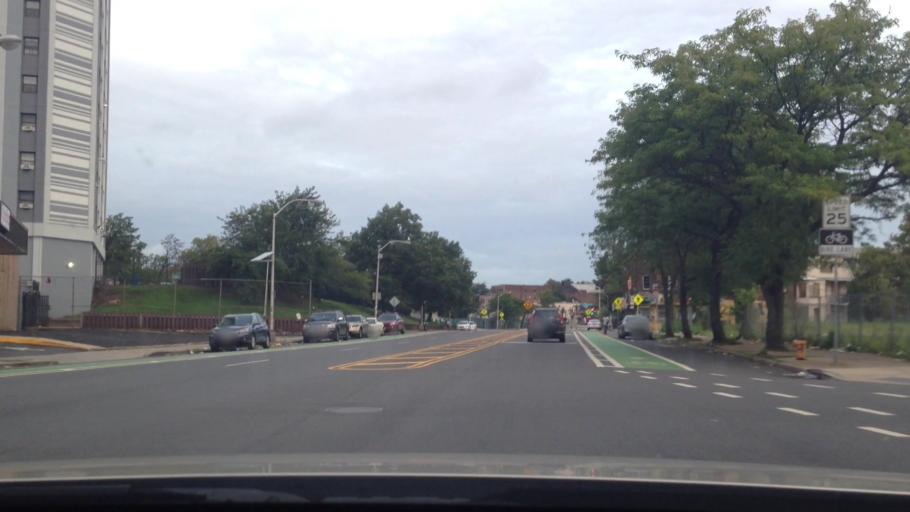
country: US
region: New Jersey
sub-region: Essex County
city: Newark
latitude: 40.7460
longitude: -74.1905
